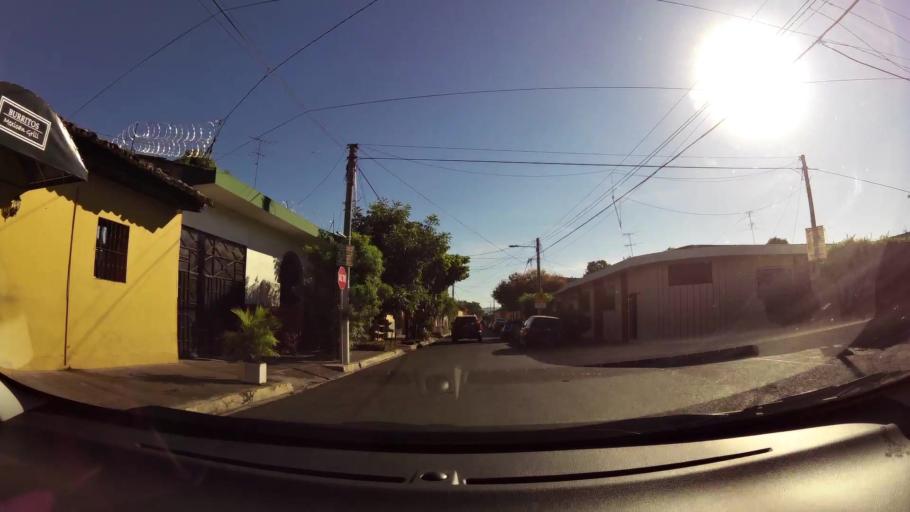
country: SV
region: San Miguel
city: San Miguel
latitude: 13.4781
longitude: -88.1822
